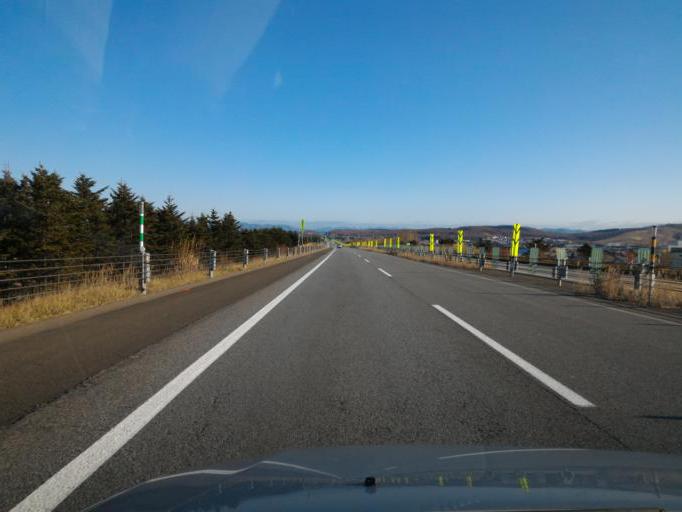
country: JP
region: Hokkaido
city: Iwamizawa
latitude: 43.1651
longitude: 141.7488
